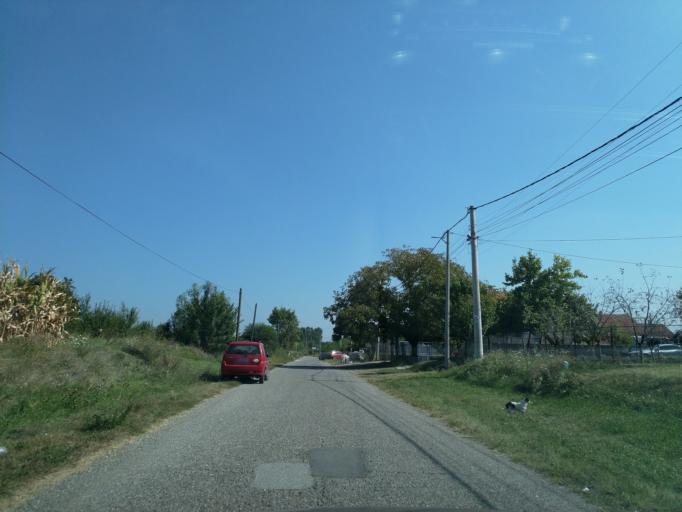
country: RS
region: Central Serbia
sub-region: Rasinski Okrug
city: Trstenik
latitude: 43.6122
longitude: 21.0254
